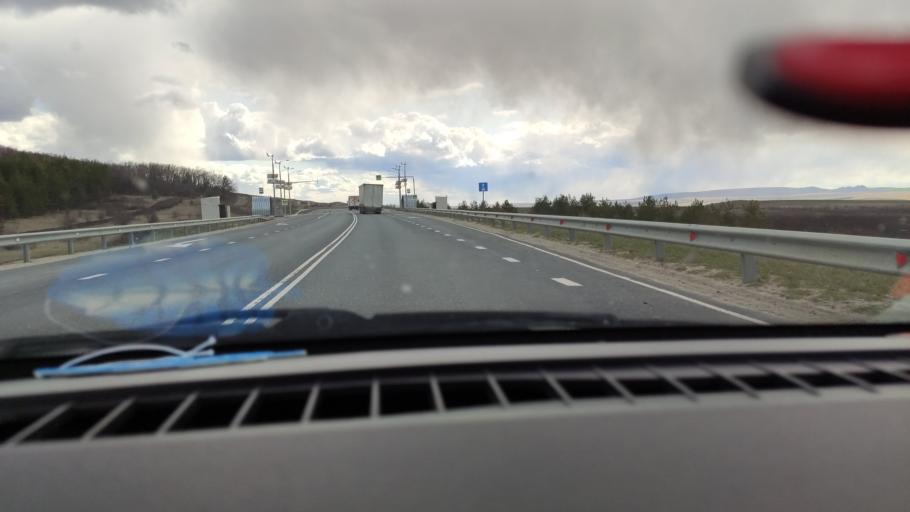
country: RU
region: Saratov
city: Alekseyevka
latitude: 52.3871
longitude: 47.9747
